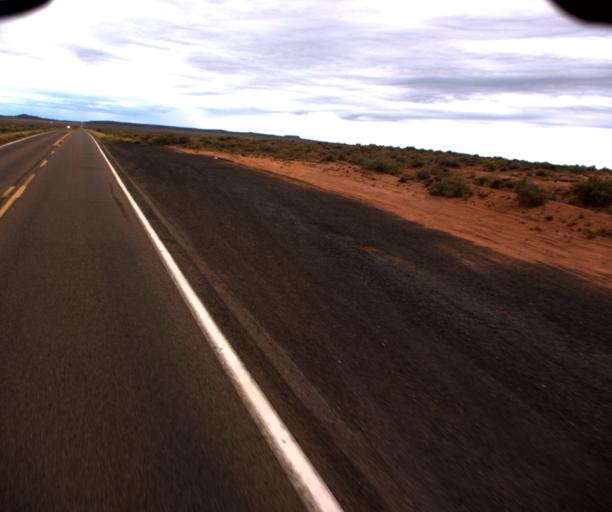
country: US
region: Arizona
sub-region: Navajo County
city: Holbrook
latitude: 34.7480
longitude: -110.1214
